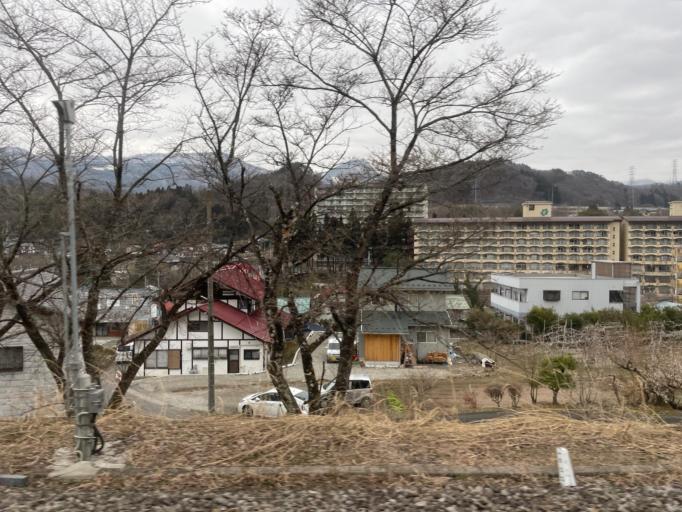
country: JP
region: Gunma
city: Numata
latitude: 36.7378
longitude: 138.9849
